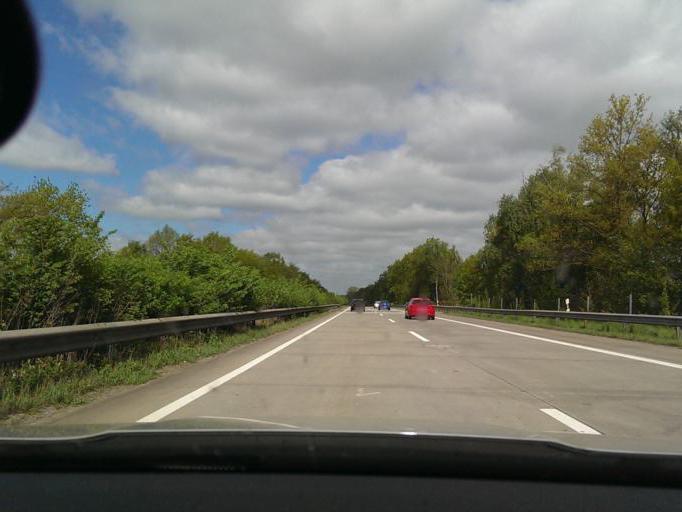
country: DE
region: Lower Saxony
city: Langwedel
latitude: 52.9721
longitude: 9.2298
